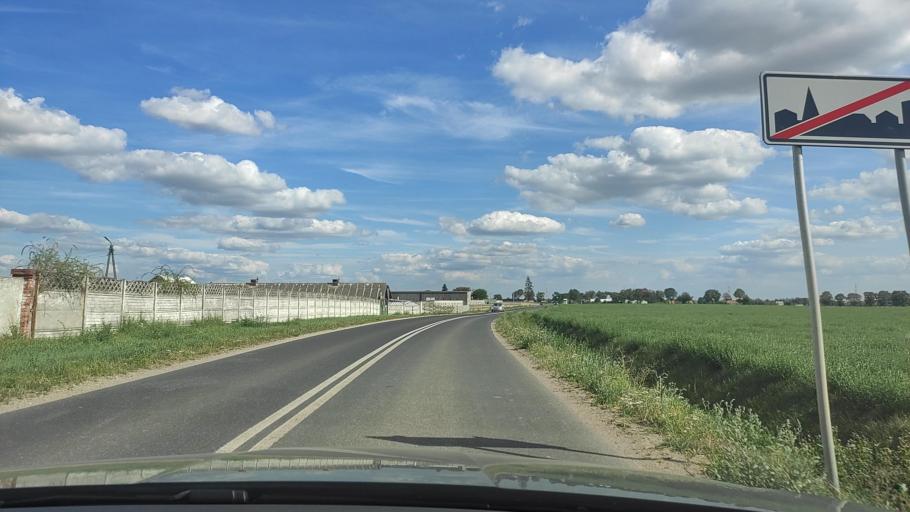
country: PL
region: Greater Poland Voivodeship
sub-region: Powiat poznanski
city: Kornik
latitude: 52.2925
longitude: 17.1086
